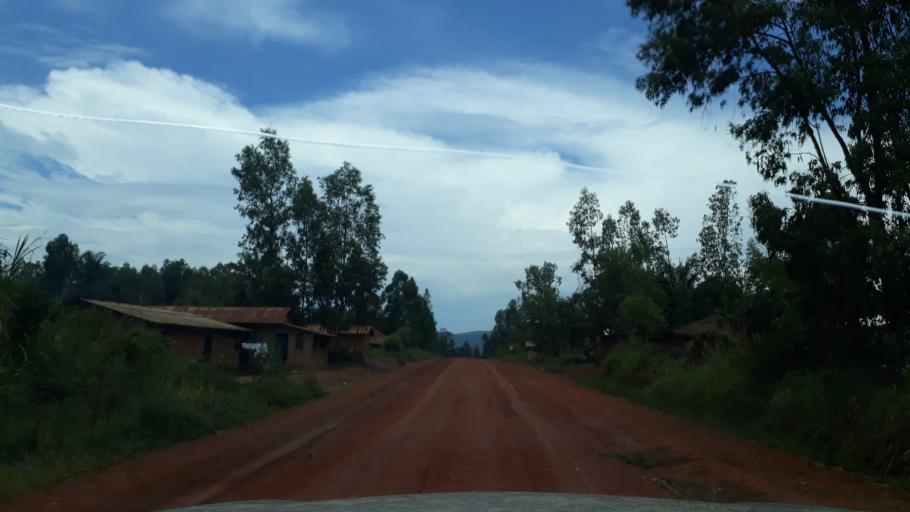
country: CD
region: Eastern Province
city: Bunia
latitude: 1.6823
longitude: 30.2778
